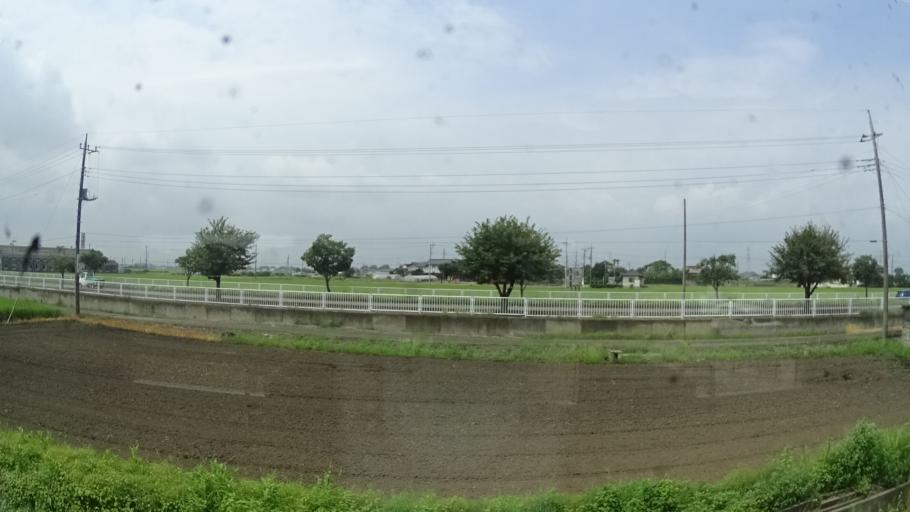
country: JP
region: Ibaraki
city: Shimodate
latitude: 36.3386
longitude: 139.9720
